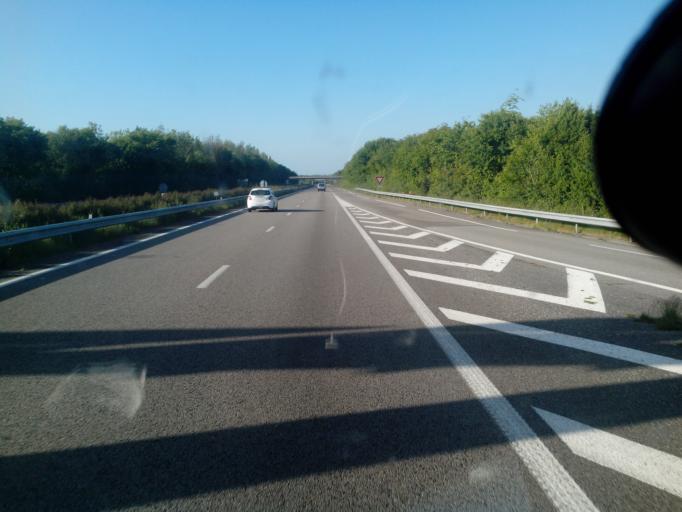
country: FR
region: Haute-Normandie
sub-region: Departement de la Seine-Maritime
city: Etainhus
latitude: 49.5553
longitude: 0.3372
